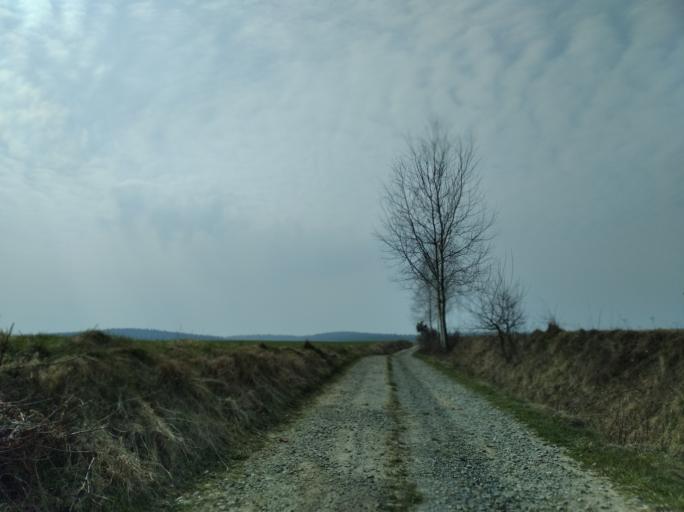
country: PL
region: Subcarpathian Voivodeship
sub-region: Powiat strzyzowski
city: Strzyzow
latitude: 49.7962
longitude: 21.8166
